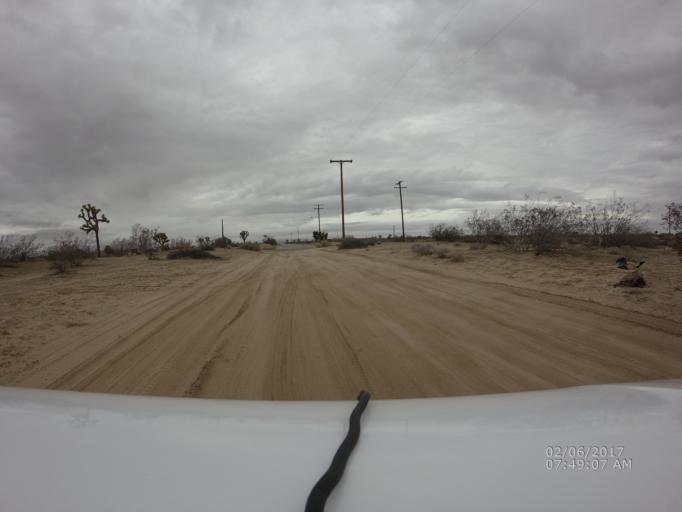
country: US
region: California
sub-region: Los Angeles County
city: Lake Los Angeles
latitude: 34.6901
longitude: -117.7741
